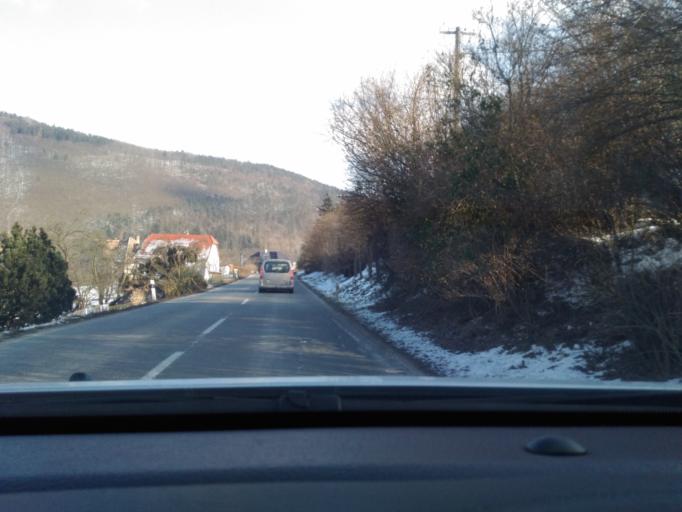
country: CZ
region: South Moravian
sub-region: Okres Brno-Venkov
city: Nedvedice
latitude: 49.4529
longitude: 16.3379
